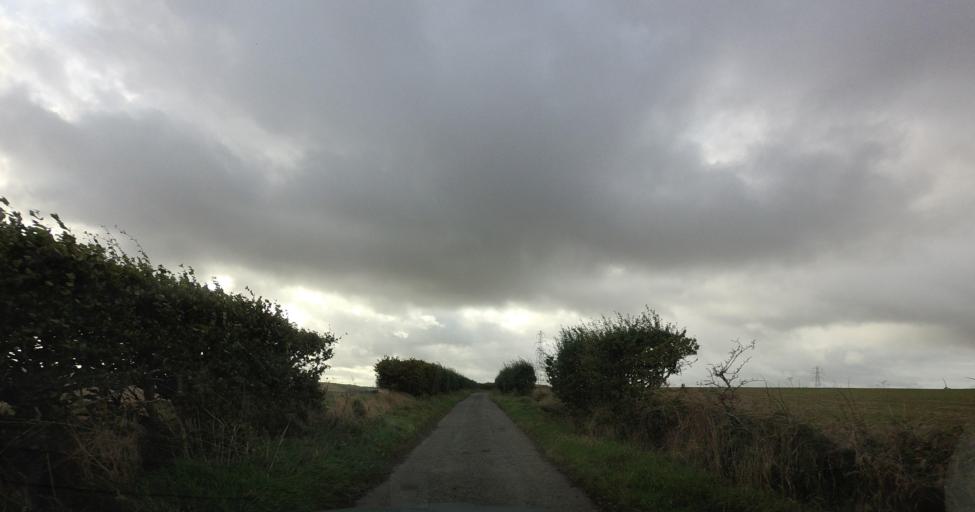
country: GB
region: Scotland
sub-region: Aberdeenshire
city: Whitehills
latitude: 57.6593
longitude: -2.6099
